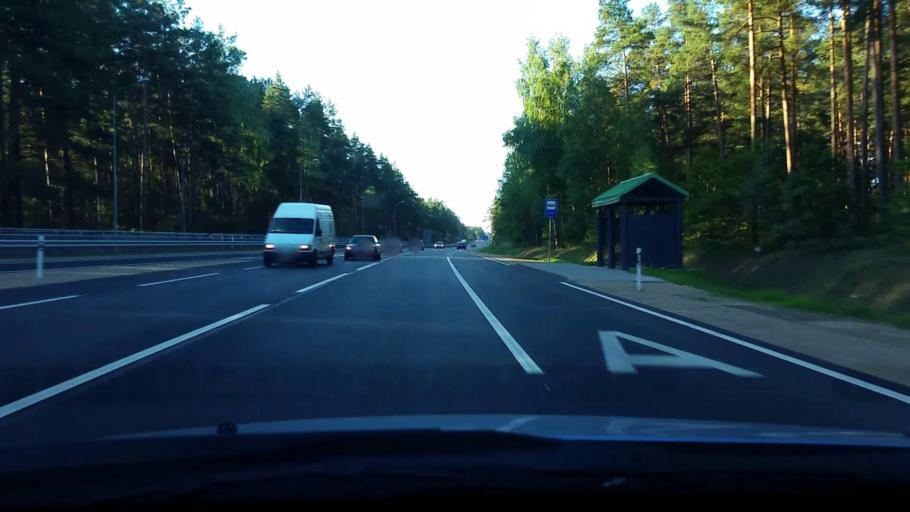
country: LV
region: Adazi
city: Adazi
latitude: 57.0587
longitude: 24.3218
